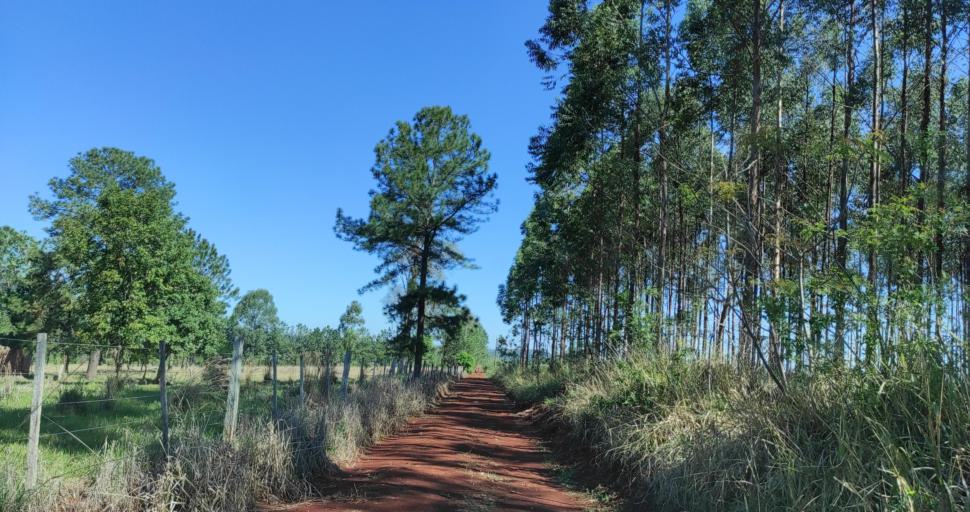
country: AR
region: Misiones
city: Capiovi
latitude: -26.9103
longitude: -55.0197
